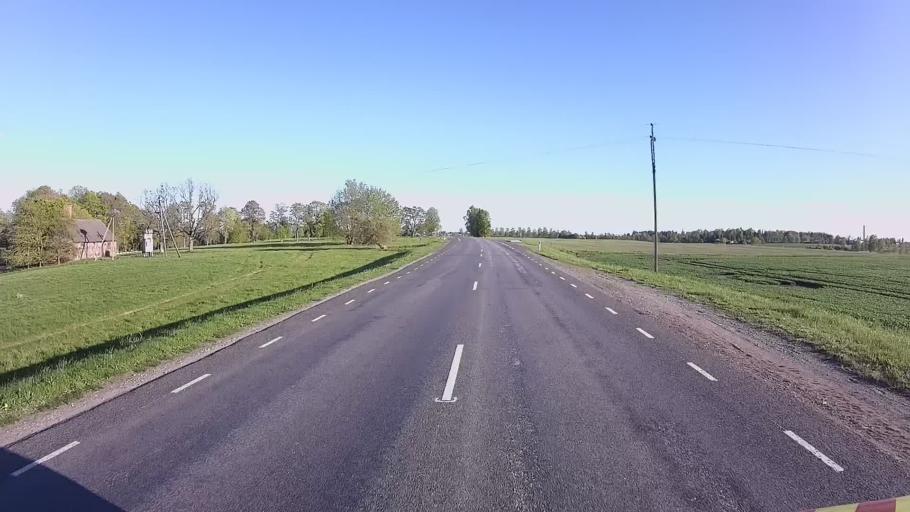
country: EE
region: Viljandimaa
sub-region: Viljandi linn
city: Viljandi
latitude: 58.3974
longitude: 25.5918
